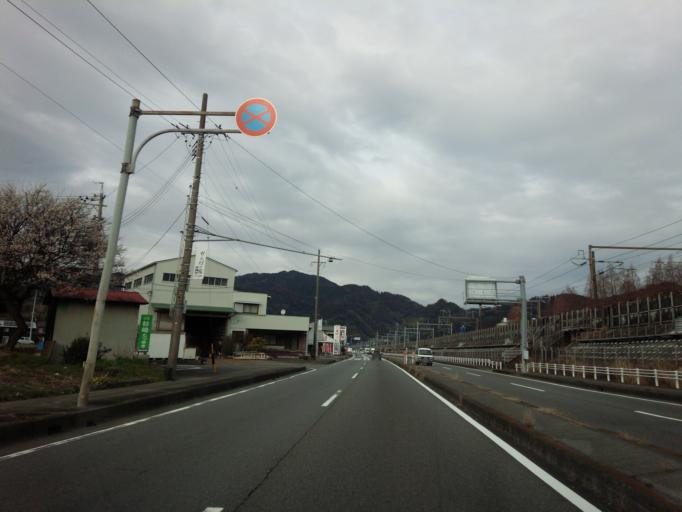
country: JP
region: Shizuoka
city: Yaizu
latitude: 34.8838
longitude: 138.3220
